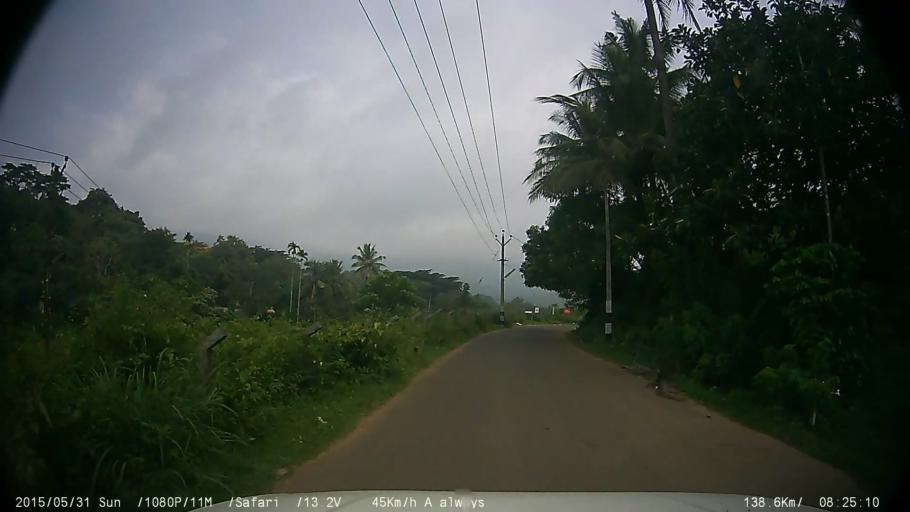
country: IN
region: Kerala
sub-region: Wayanad
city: Kalpetta
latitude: 11.6748
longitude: 75.9590
